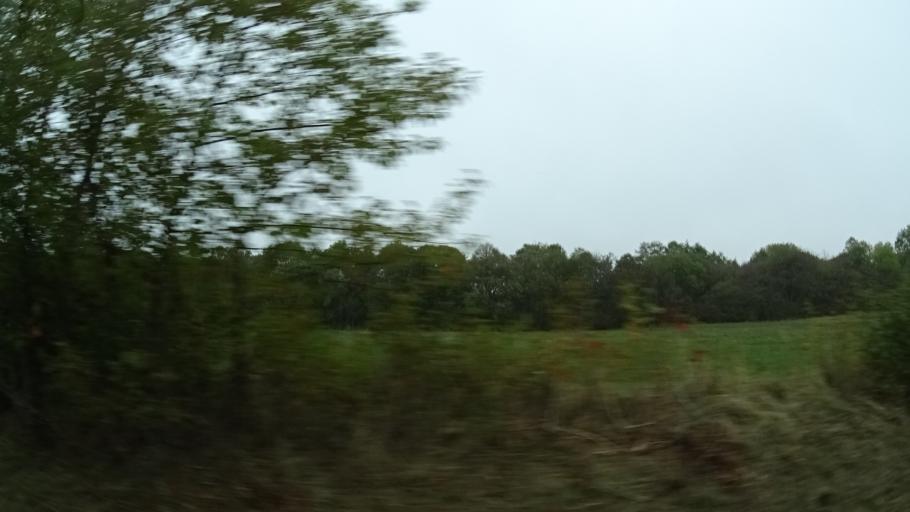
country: DE
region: Hesse
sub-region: Regierungsbezirk Kassel
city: Hilders
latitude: 50.5666
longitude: 10.0169
